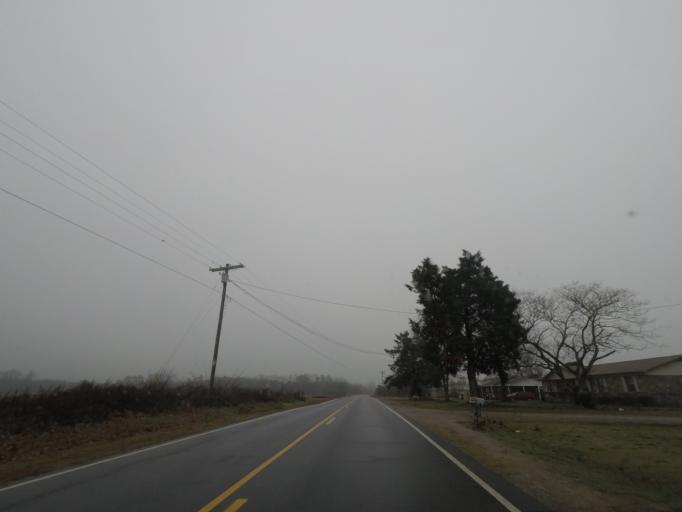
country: US
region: North Carolina
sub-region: Scotland County
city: Laurinburg
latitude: 34.8060
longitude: -79.4409
